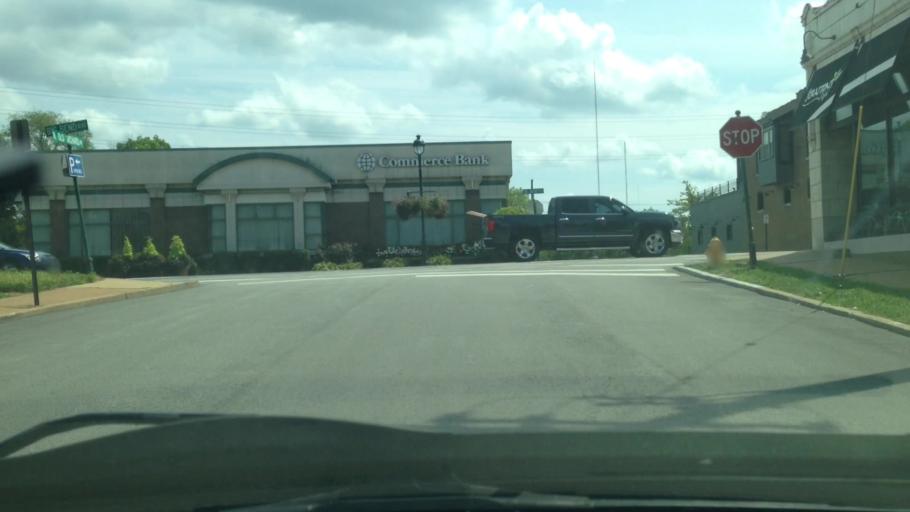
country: US
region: Missouri
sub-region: Saint Louis County
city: Shrewsbury
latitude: 38.5923
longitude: -90.3379
